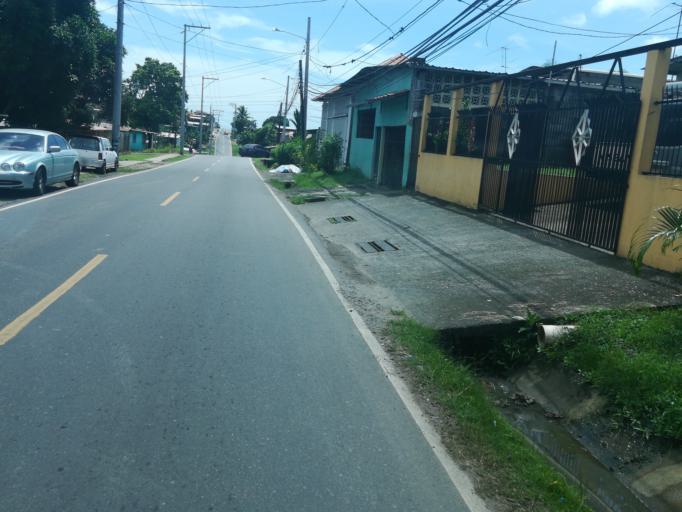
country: PA
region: Panama
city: Tocumen
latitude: 9.0948
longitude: -79.4058
